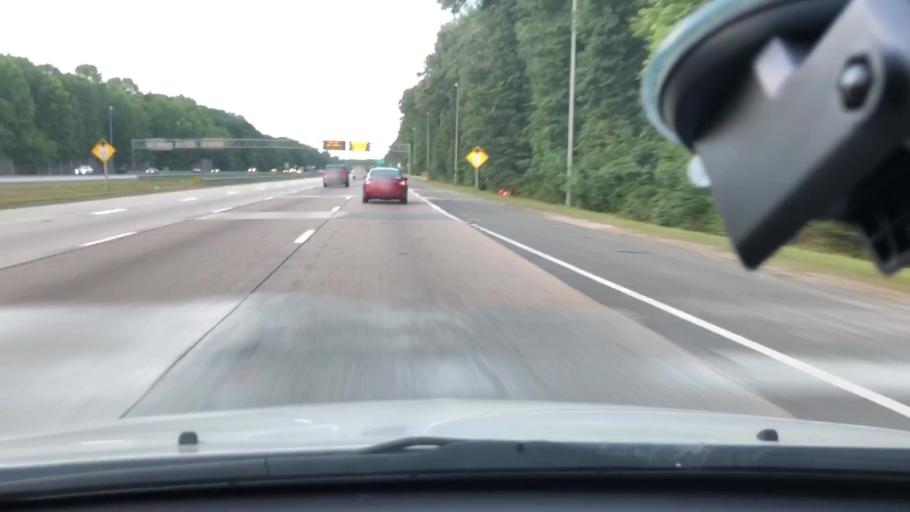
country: US
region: Virginia
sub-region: City of Chesapeake
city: Chesapeake
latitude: 36.7921
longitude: -76.2146
